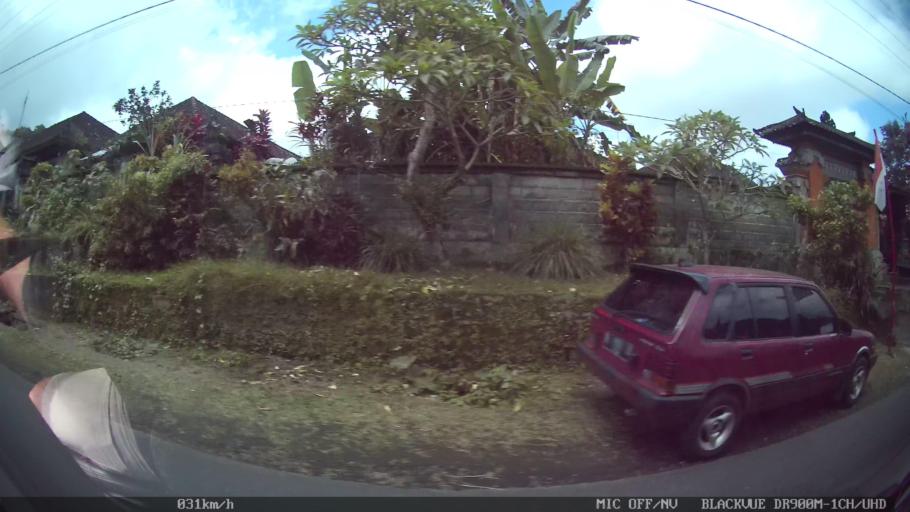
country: ID
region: Bali
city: Banjar Abuan
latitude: -8.4549
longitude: 115.3408
